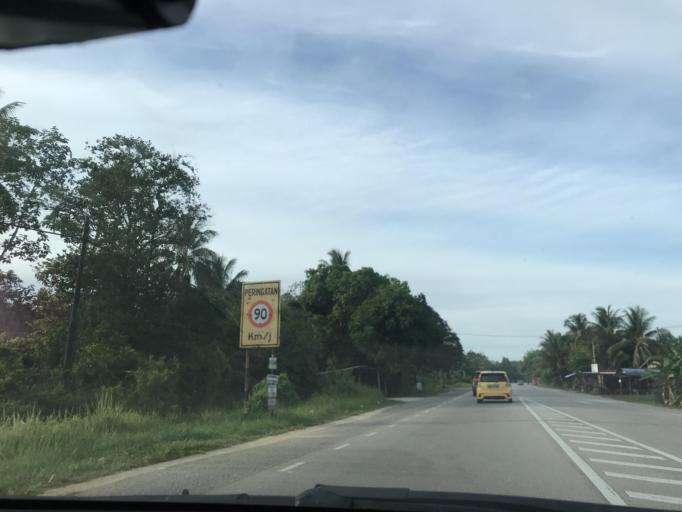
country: MY
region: Kelantan
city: Kampong Pangkal Kalong
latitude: 5.9667
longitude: 102.1936
